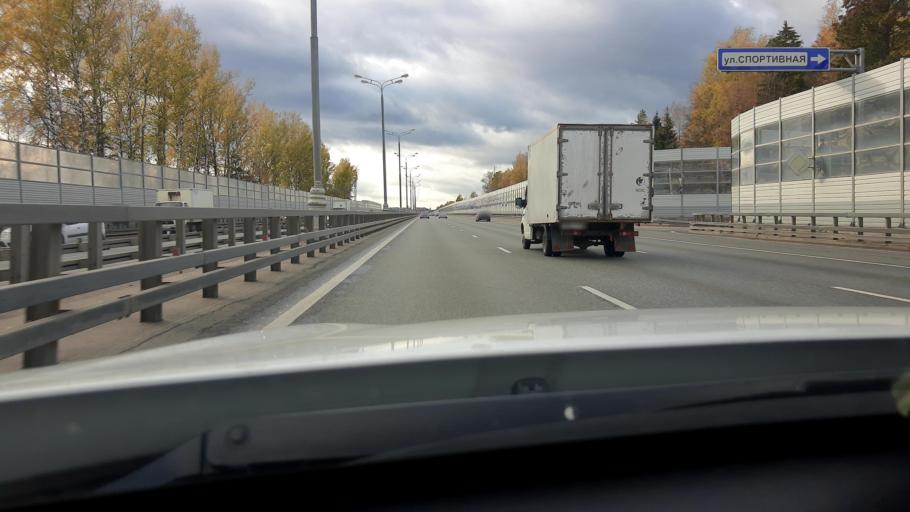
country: RU
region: Moskovskaya
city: Aprelevka
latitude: 55.5309
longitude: 37.0487
